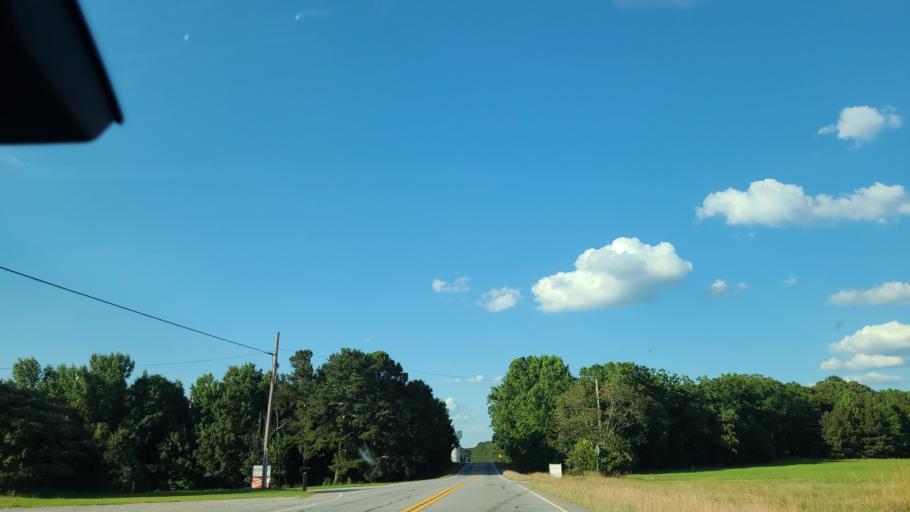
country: US
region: Georgia
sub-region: Oconee County
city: Watkinsville
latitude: 33.8393
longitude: -83.4275
